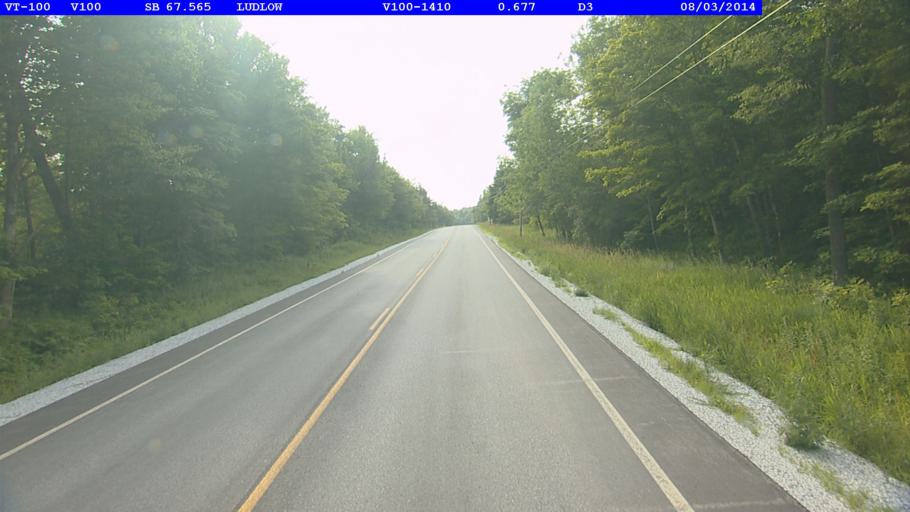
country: US
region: Vermont
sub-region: Windsor County
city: Chester
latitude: 43.3537
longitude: -72.7450
